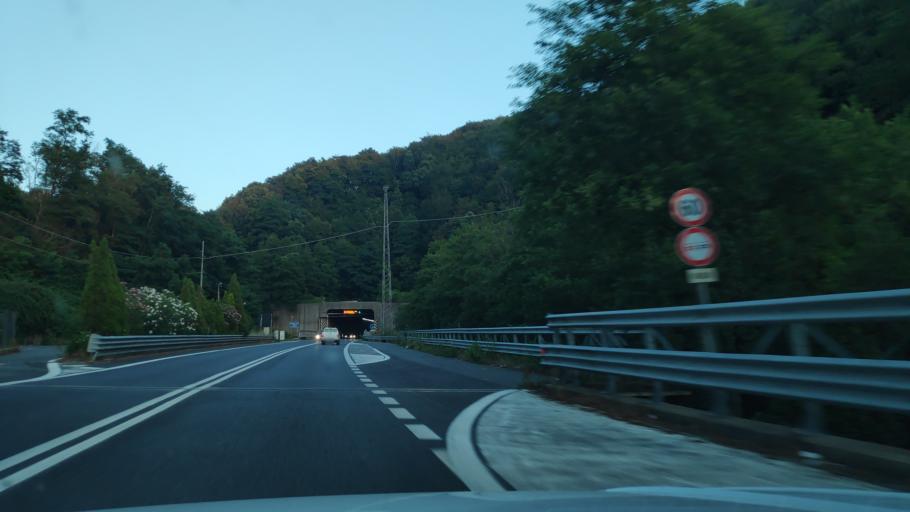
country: IT
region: Calabria
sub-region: Provincia di Reggio Calabria
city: Amato
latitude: 38.4021
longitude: 16.1621
